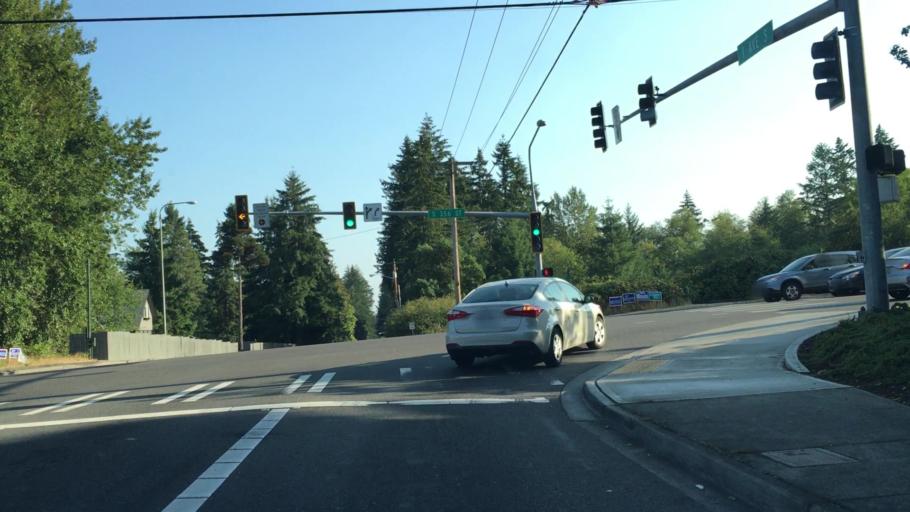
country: US
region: Washington
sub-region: Pierce County
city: Fife Heights
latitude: 47.2829
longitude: -122.3348
